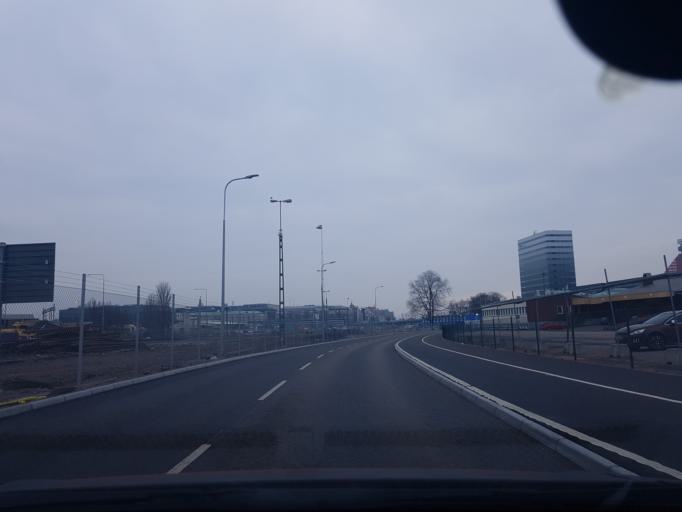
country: SE
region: Vaestra Goetaland
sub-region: Goteborg
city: Goeteborg
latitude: 57.7125
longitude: 11.9785
